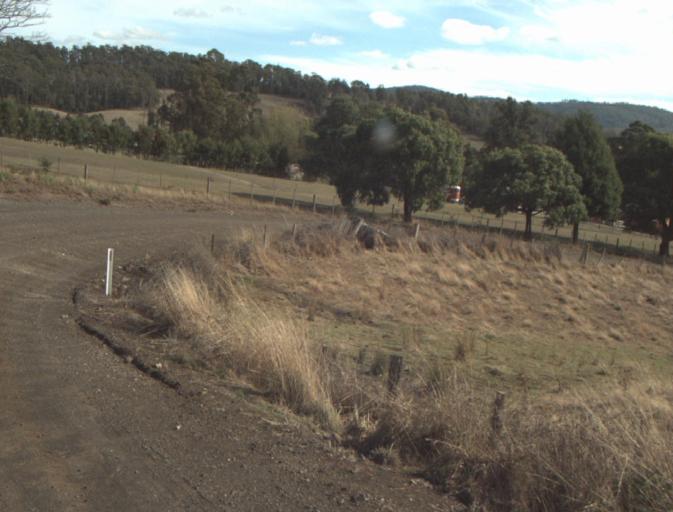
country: AU
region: Tasmania
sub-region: Launceston
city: Mayfield
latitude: -41.2185
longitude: 147.1672
